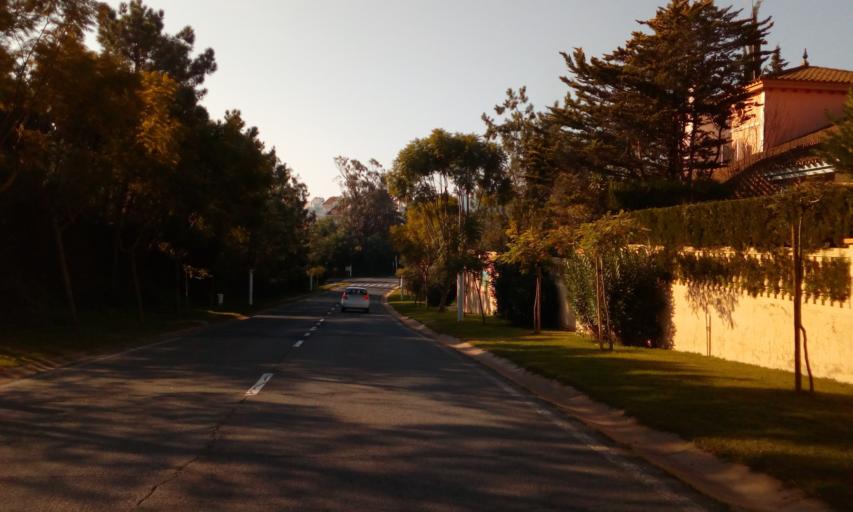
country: ES
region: Andalusia
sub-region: Provincia de Huelva
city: Lepe
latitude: 37.2116
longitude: -7.2322
